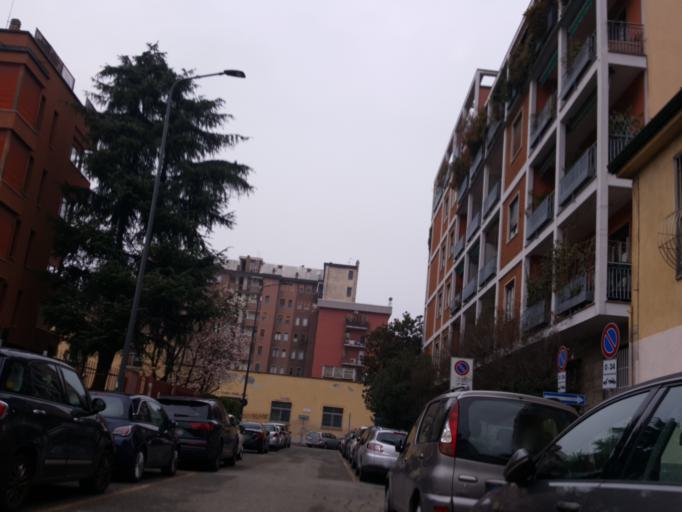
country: IT
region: Lombardy
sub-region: Citta metropolitana di Milano
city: Milano
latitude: 45.4584
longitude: 9.1593
